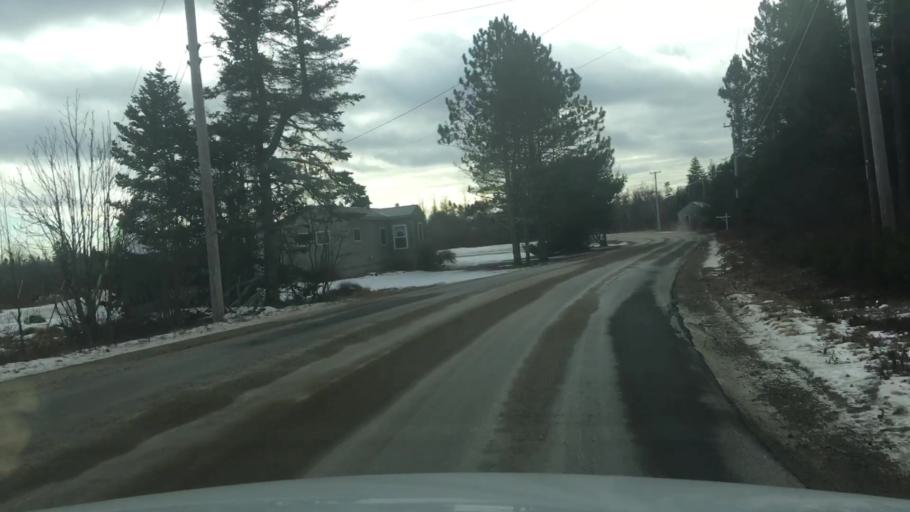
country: US
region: Maine
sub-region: Washington County
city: Machias
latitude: 44.6209
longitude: -67.4789
